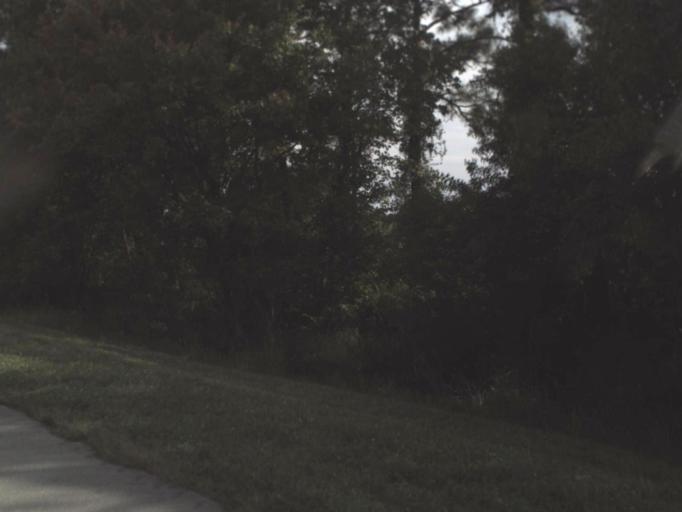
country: US
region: Florida
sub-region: Okeechobee County
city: Taylor Creek
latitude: 27.1738
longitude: -80.6997
